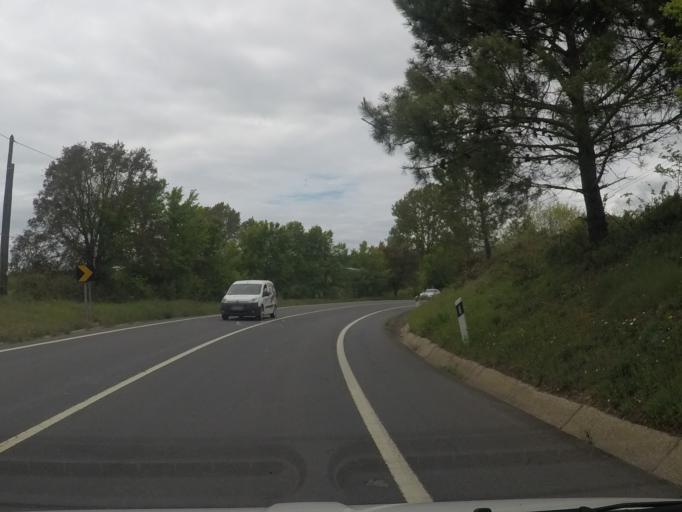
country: PT
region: Setubal
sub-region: Santiago do Cacem
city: Cercal
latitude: 37.8268
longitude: -8.6970
